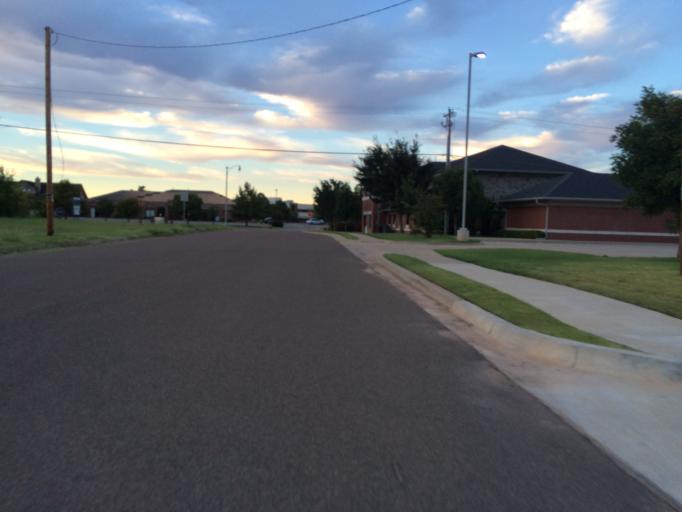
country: US
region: Oklahoma
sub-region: Cleveland County
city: Norman
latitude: 35.2253
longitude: -97.4796
